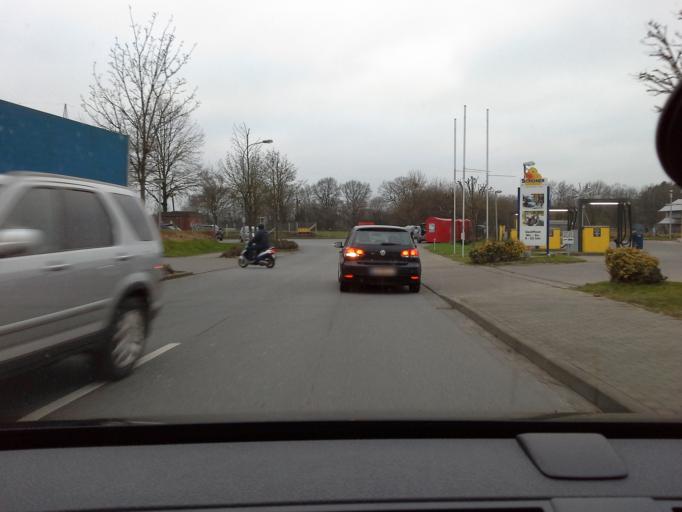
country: DE
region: Schleswig-Holstein
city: Quickborn
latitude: 53.7219
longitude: 9.9018
